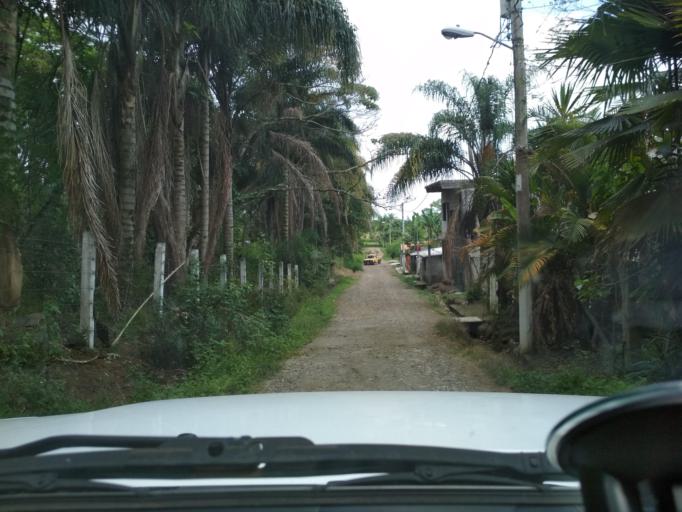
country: MX
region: Veracruz
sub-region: Fortin
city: Monte Salas
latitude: 18.9369
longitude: -97.0149
